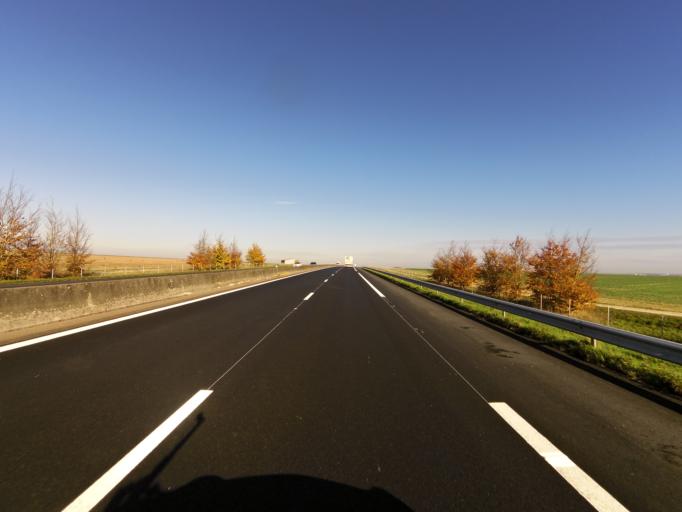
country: FR
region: Champagne-Ardenne
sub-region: Departement de la Marne
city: Fagnieres
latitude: 48.9232
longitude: 4.2833
